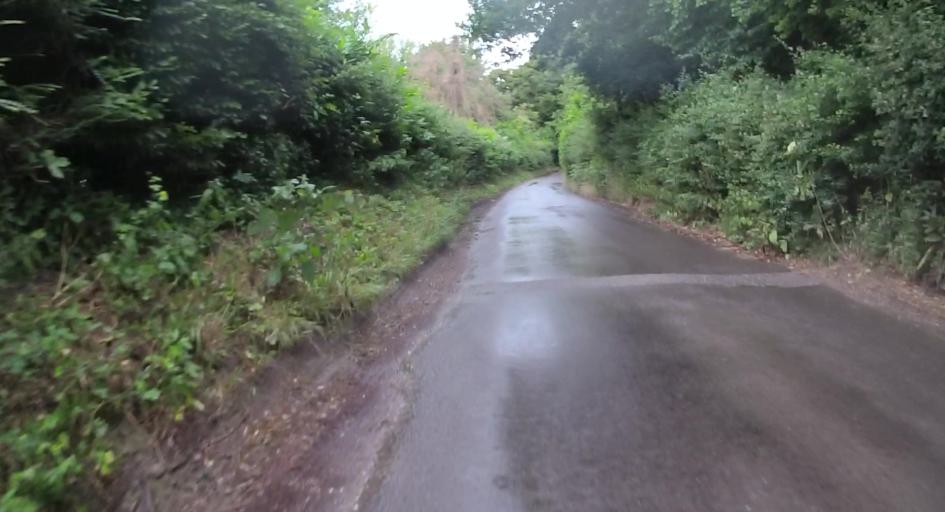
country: GB
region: England
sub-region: Hampshire
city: Long Sutton
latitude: 51.1704
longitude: -0.9202
